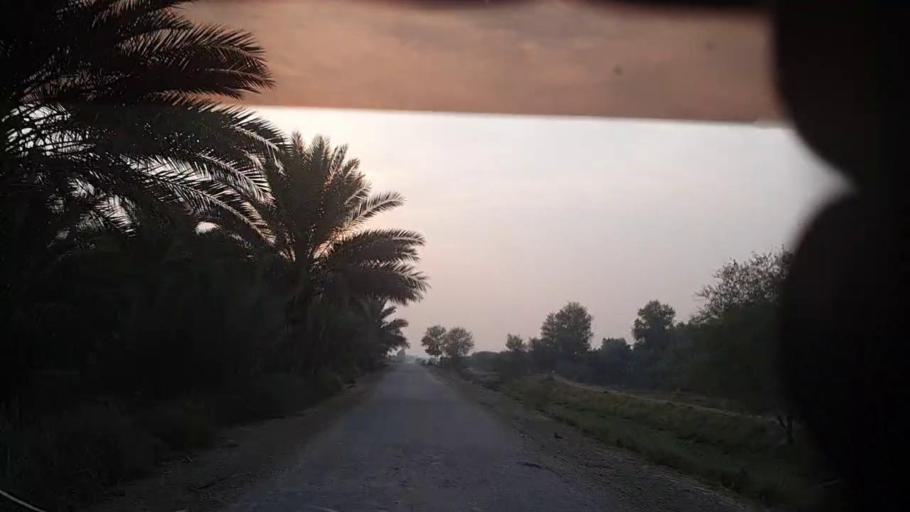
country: PK
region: Sindh
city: Pir jo Goth
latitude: 27.5259
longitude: 68.6634
